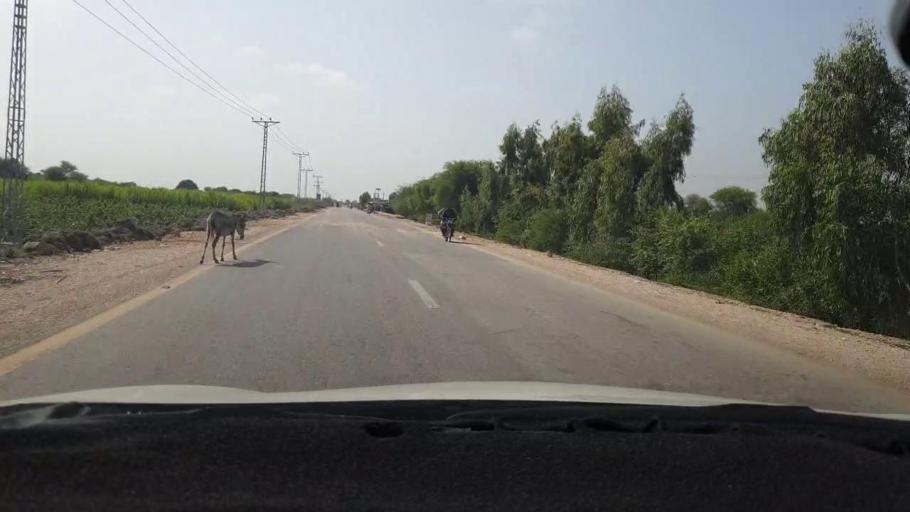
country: PK
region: Sindh
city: Mirpur Khas
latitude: 25.7736
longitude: 69.0712
